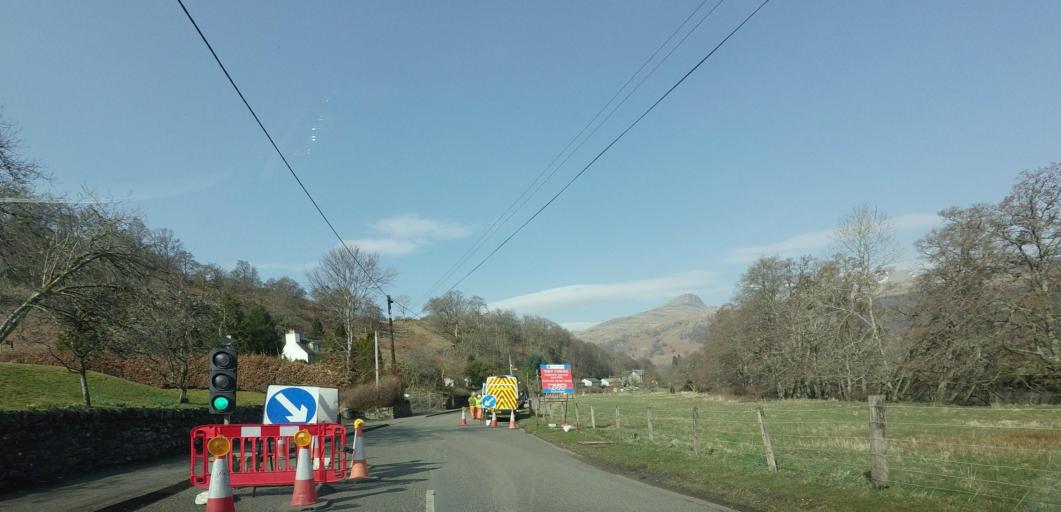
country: GB
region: Scotland
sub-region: Stirling
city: Callander
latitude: 56.4702
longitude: -4.3197
